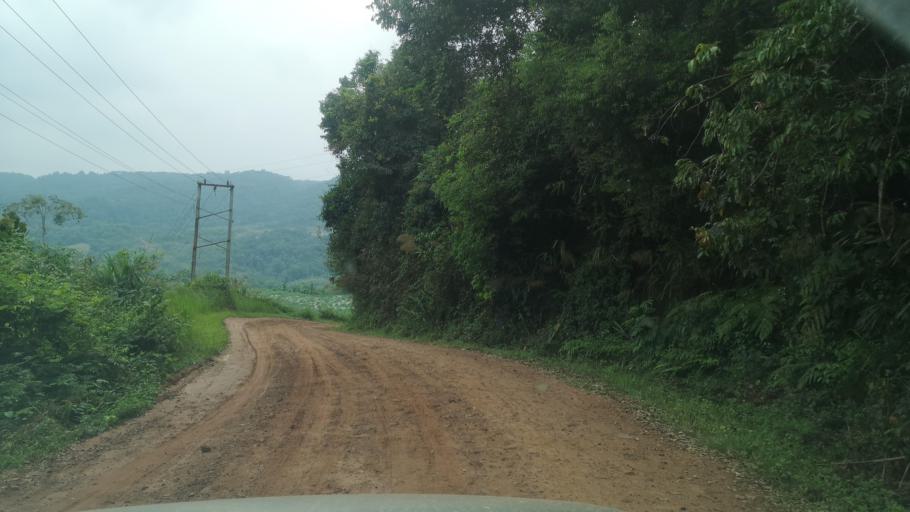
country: LA
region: Oudomxai
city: Muang La
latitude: 21.1073
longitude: 101.8688
